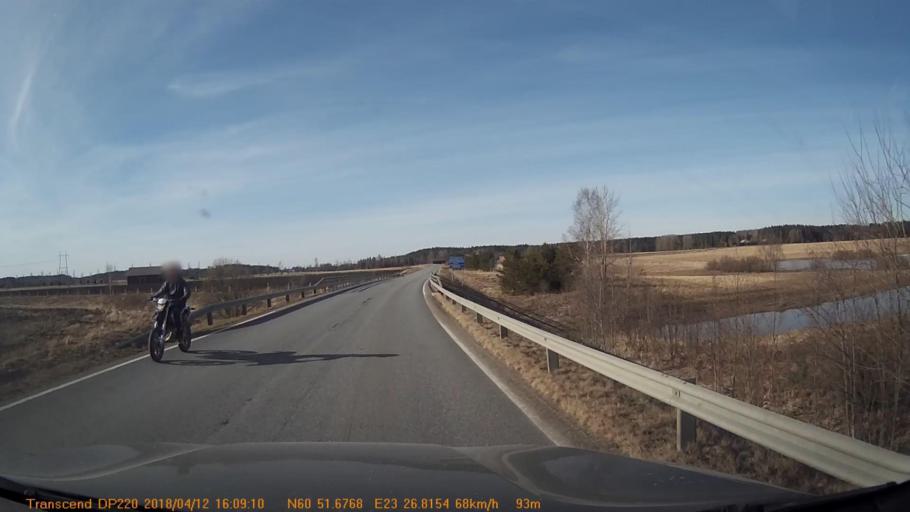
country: FI
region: Haeme
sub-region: Forssa
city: Jokioinen
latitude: 60.8612
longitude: 23.4470
